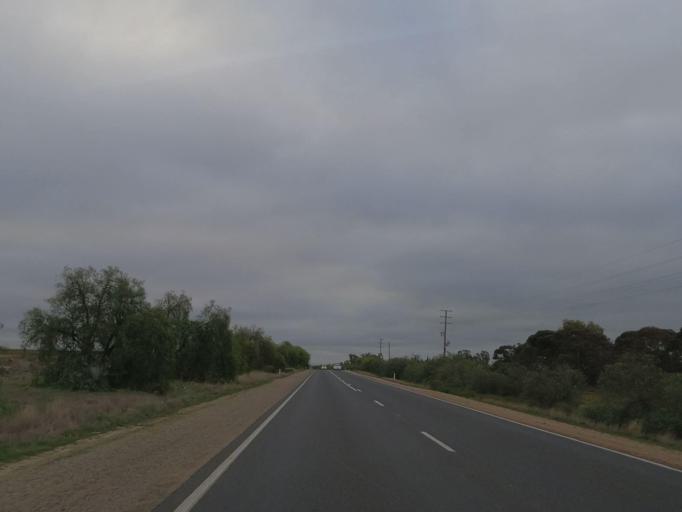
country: AU
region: Victoria
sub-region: Swan Hill
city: Swan Hill
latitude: -35.4475
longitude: 143.6215
